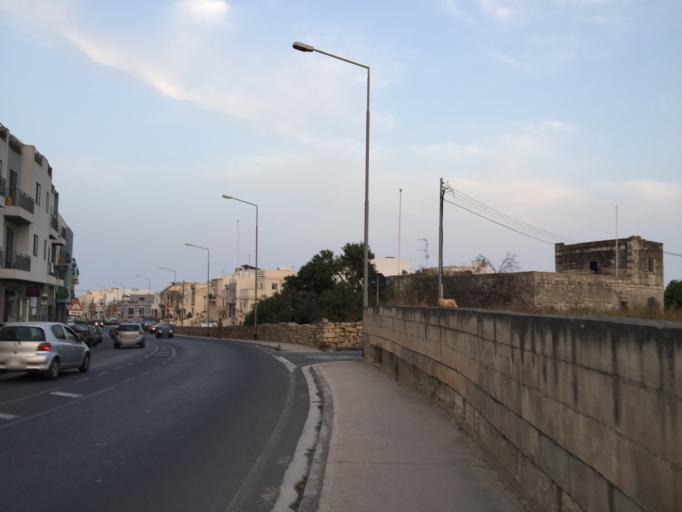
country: MT
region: Haz-Zabbar
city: Zabbar
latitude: 35.8714
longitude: 14.5333
